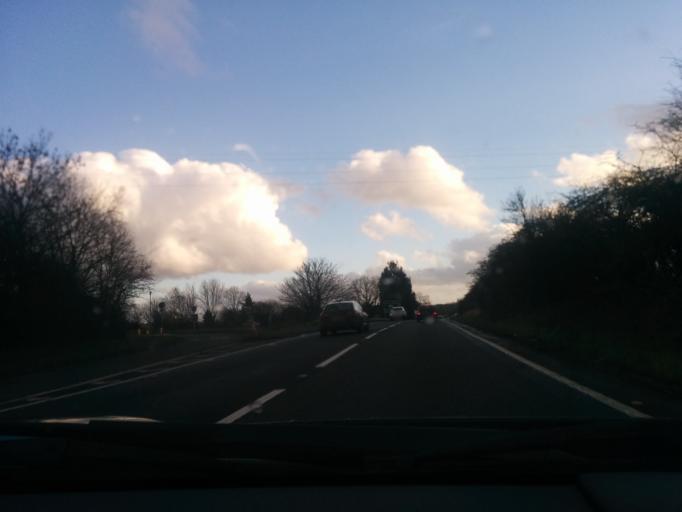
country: GB
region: England
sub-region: Oxfordshire
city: Oxford
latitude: 51.7349
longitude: -1.2688
